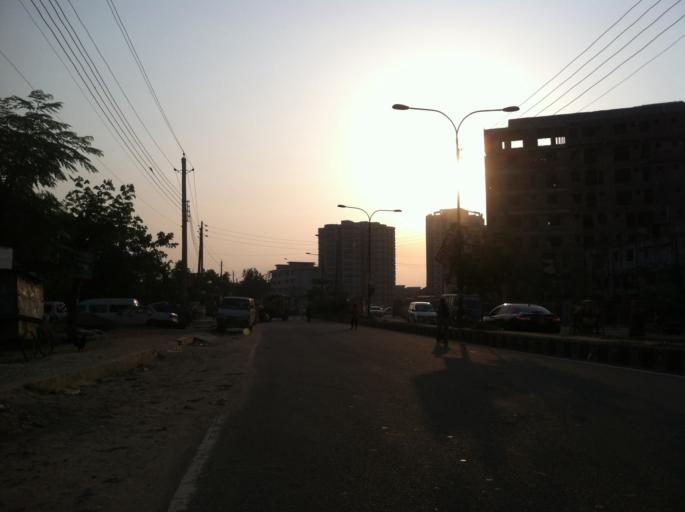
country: BD
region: Dhaka
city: Tungi
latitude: 23.8221
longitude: 90.3920
